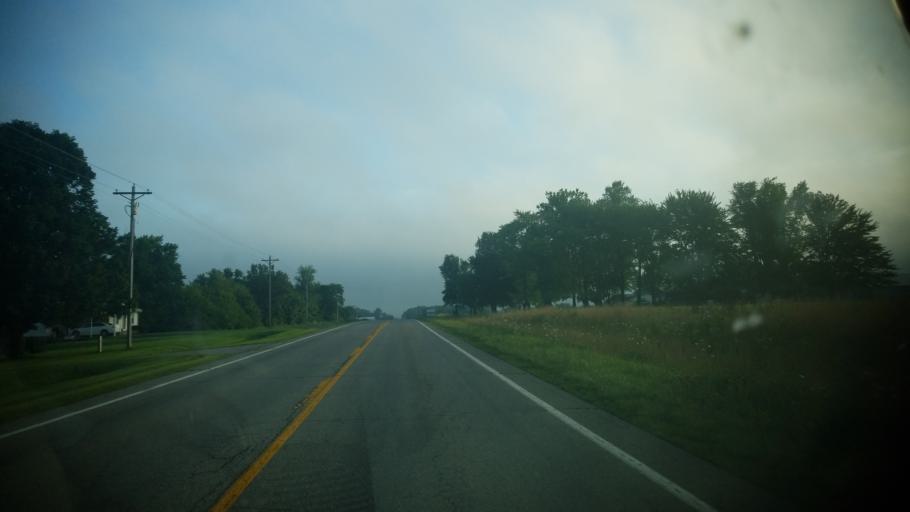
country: US
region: Illinois
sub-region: Wayne County
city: Fairfield
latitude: 38.3848
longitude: -88.4057
